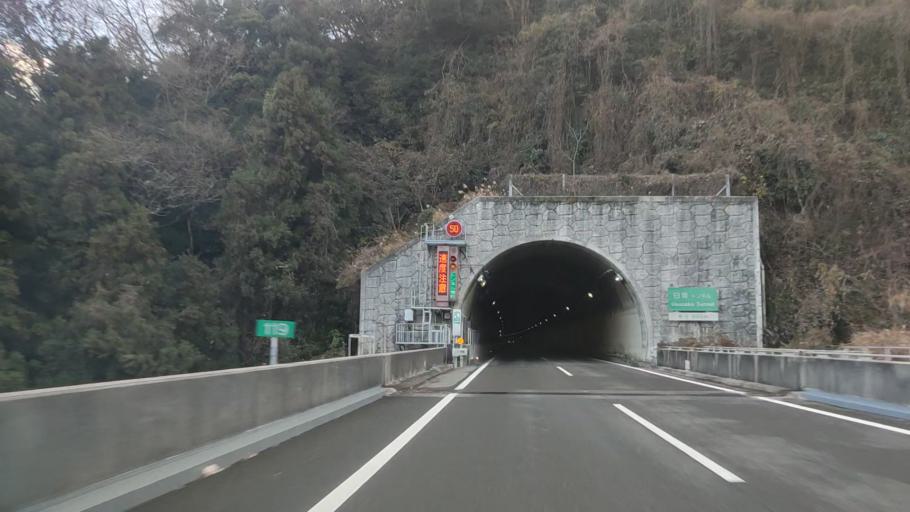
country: JP
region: Ehime
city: Saijo
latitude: 33.8450
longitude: 132.9927
